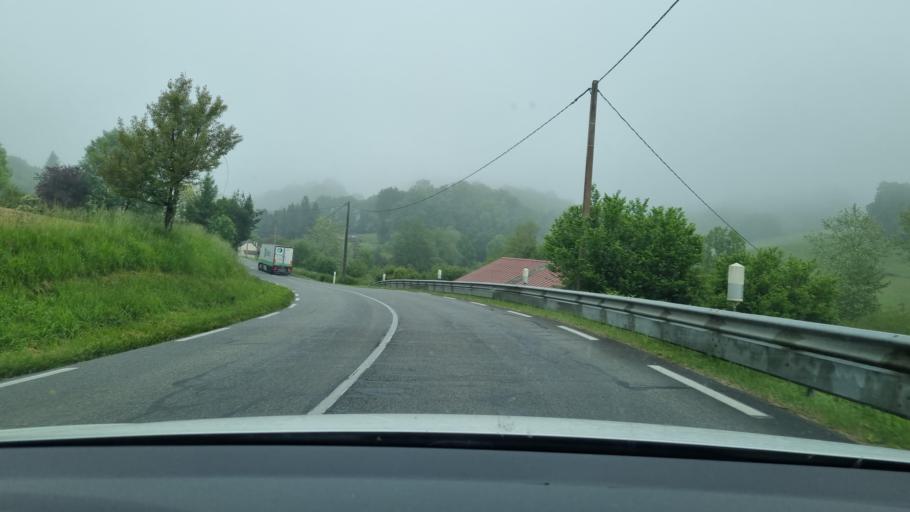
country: FR
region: Aquitaine
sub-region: Departement des Pyrenees-Atlantiques
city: Orthez
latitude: 43.5122
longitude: -0.7261
